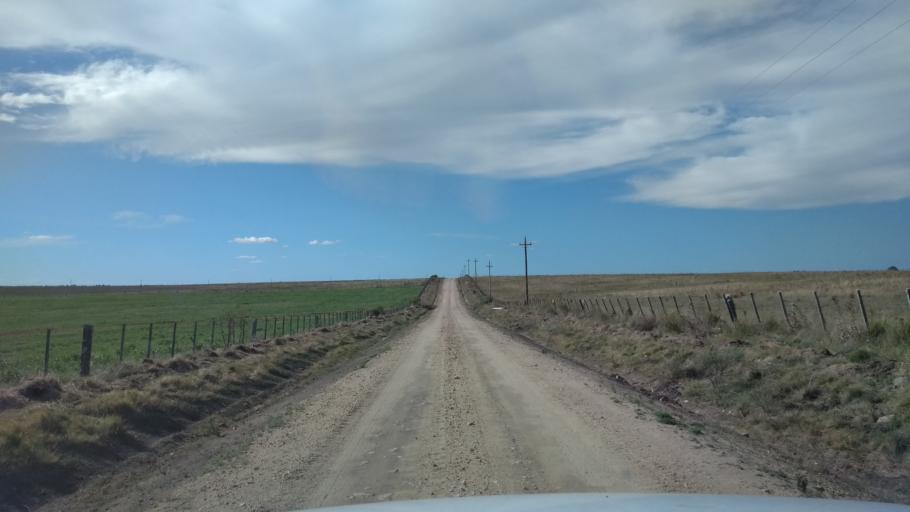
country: UY
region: Florida
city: Casupa
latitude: -34.0093
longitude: -55.7870
